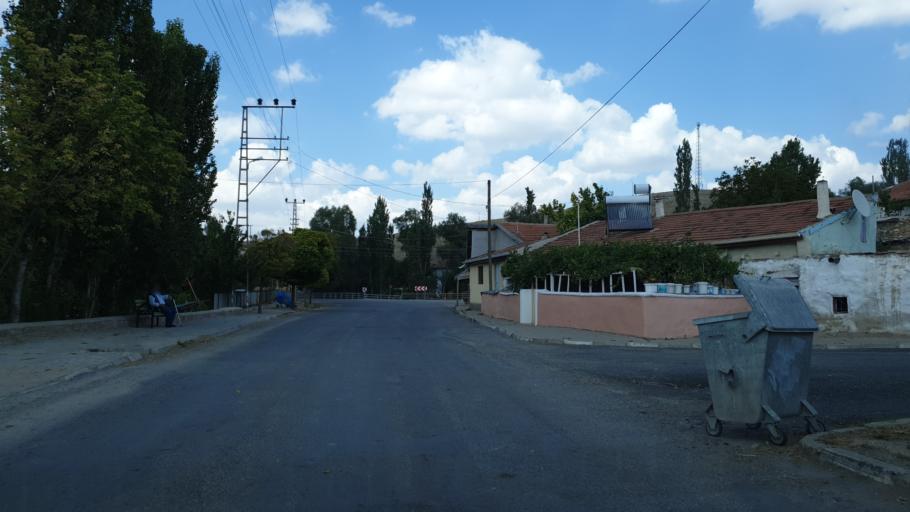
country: TR
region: Kayseri
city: Felahiye
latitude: 39.0930
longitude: 35.5631
